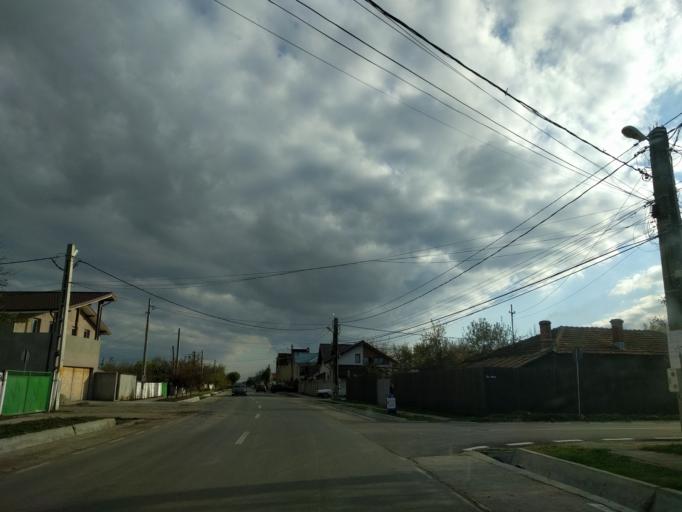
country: RO
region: Ilfov
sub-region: Comuna Branesti
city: Branesti
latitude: 44.4523
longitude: 26.3441
